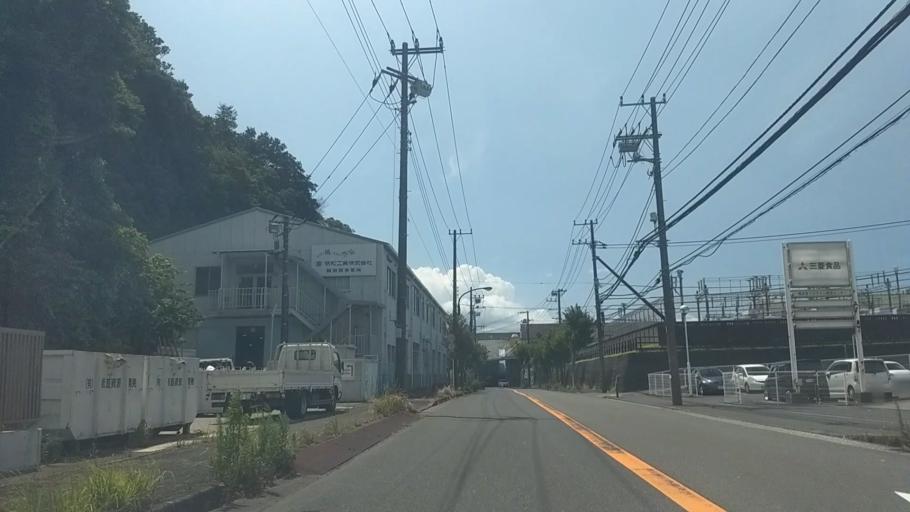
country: JP
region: Kanagawa
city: Yokosuka
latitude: 35.3143
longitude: 139.6411
